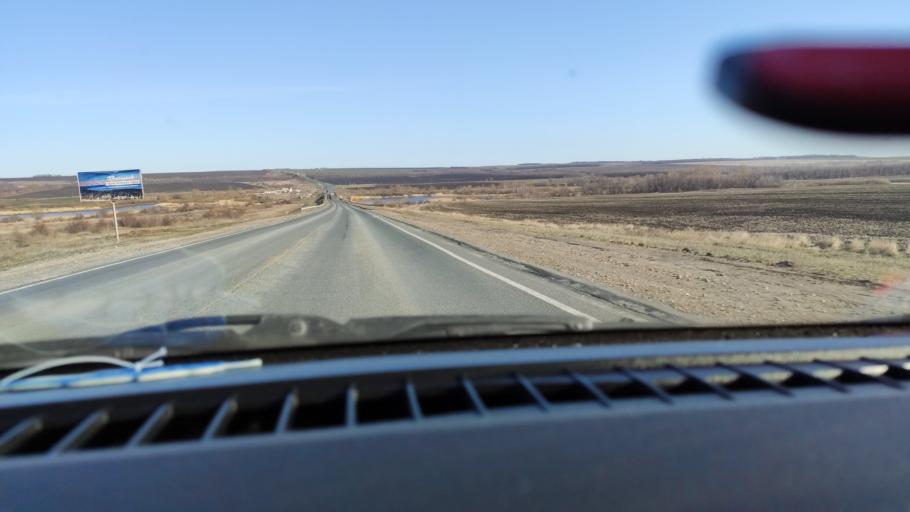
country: RU
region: Saratov
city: Dukhovnitskoye
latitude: 52.7320
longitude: 48.2579
